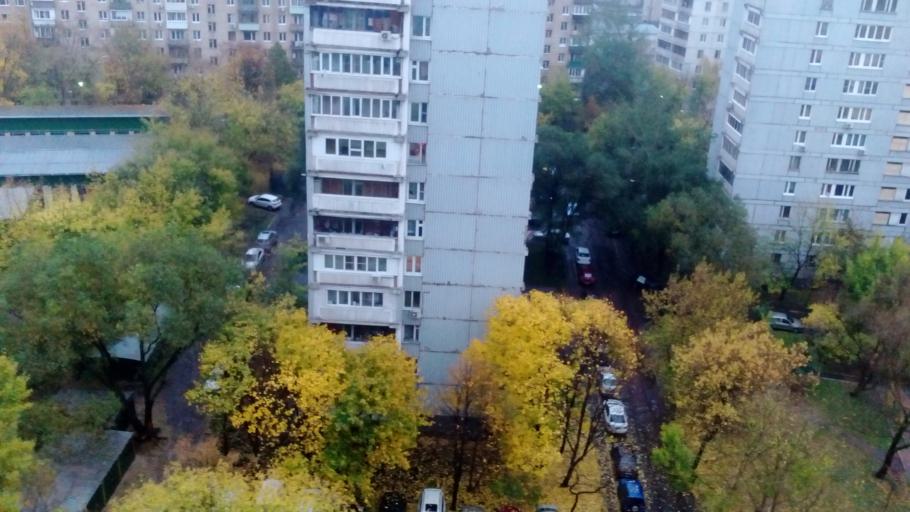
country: RU
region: Moscow
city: Mar'ina Roshcha
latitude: 55.8021
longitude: 37.5717
